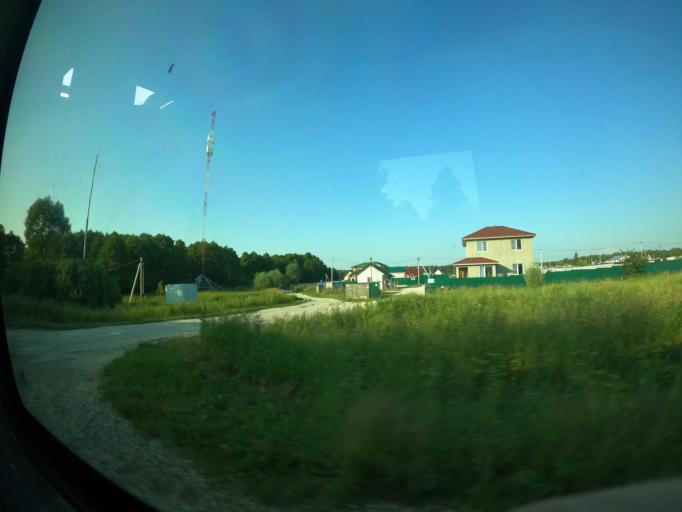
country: RU
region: Moskovskaya
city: Obolensk
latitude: 54.9409
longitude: 37.2422
